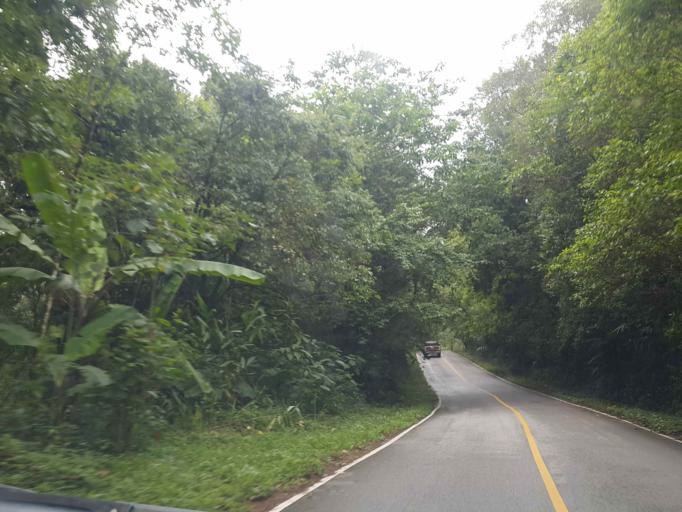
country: TH
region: Chiang Mai
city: Mae Chaem
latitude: 18.5132
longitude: 98.4774
